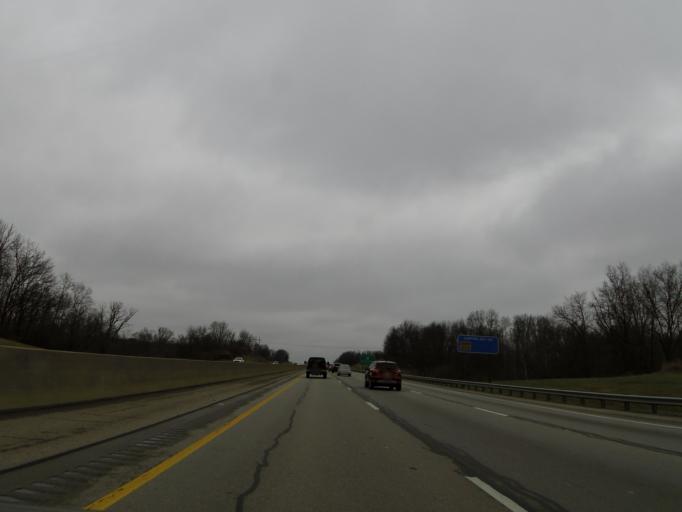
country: US
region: Kentucky
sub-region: Grant County
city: Crittenden
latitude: 38.8094
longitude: -84.6022
